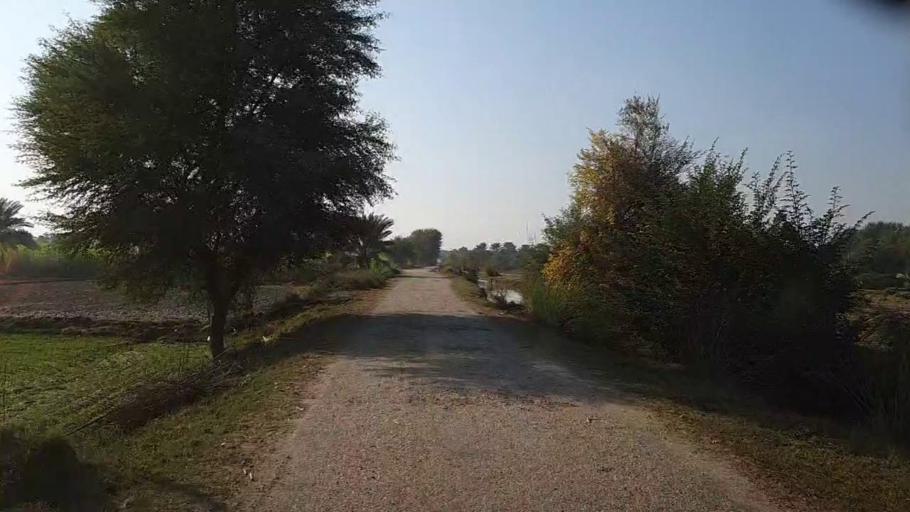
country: PK
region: Sindh
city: Ranipur
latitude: 27.2516
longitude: 68.5513
